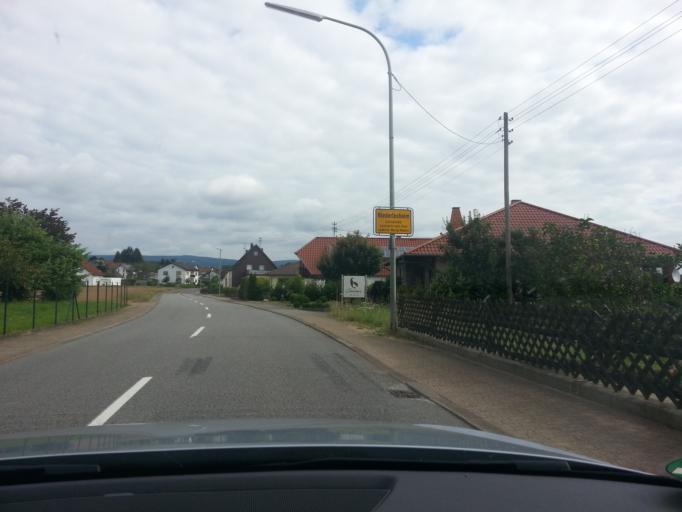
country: DE
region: Saarland
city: Losheim
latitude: 49.4959
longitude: 6.7750
